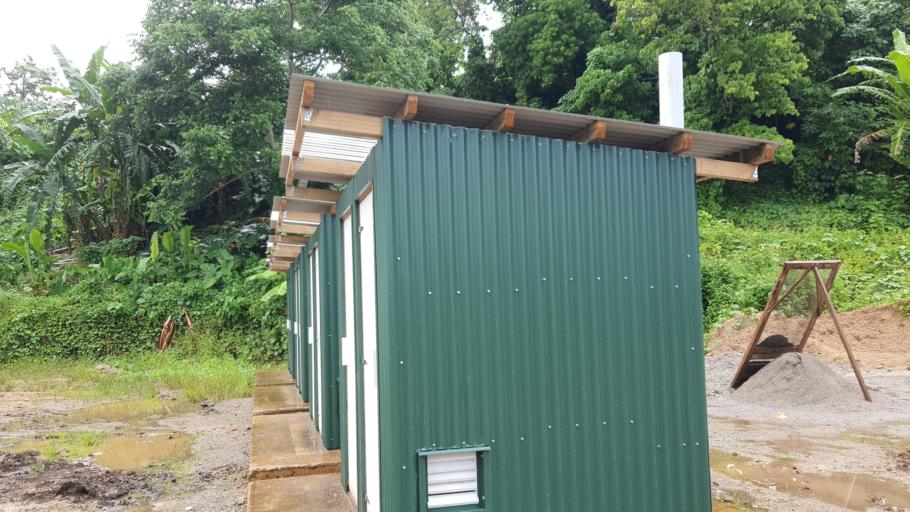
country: VU
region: Malampa
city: Lakatoro
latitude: -16.5007
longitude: 167.6508
